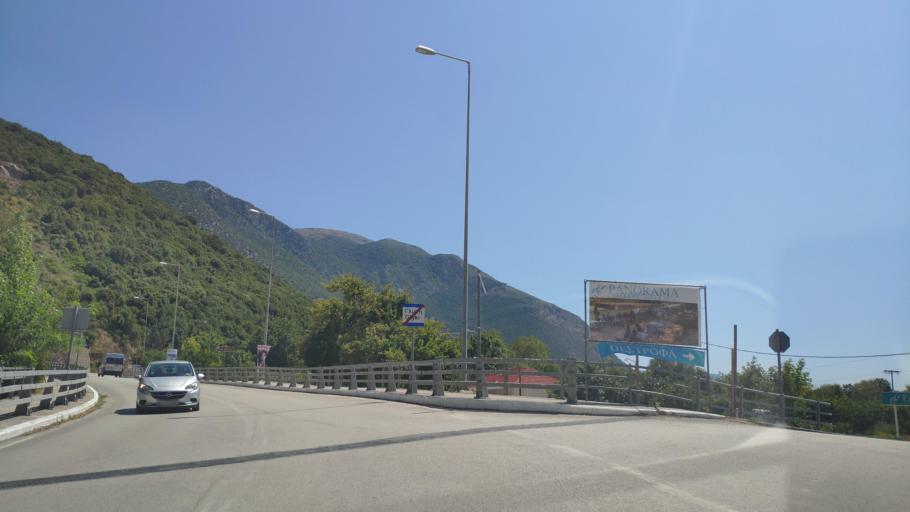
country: GR
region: Epirus
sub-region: Nomos Prevezis
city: Kanalaki
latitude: 39.3232
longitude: 20.6073
